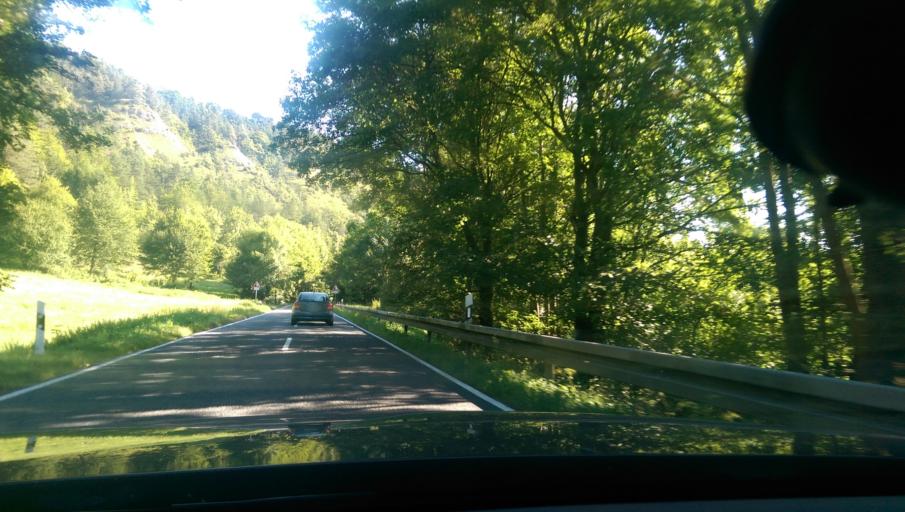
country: DE
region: Thuringia
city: Creuzburg
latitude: 51.0597
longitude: 10.2515
